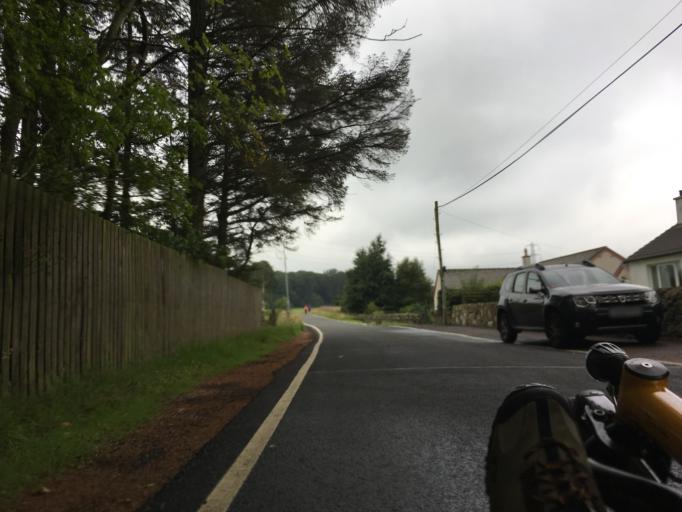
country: GB
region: Scotland
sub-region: West Lothian
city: West Calder
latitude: 55.8423
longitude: -3.5230
